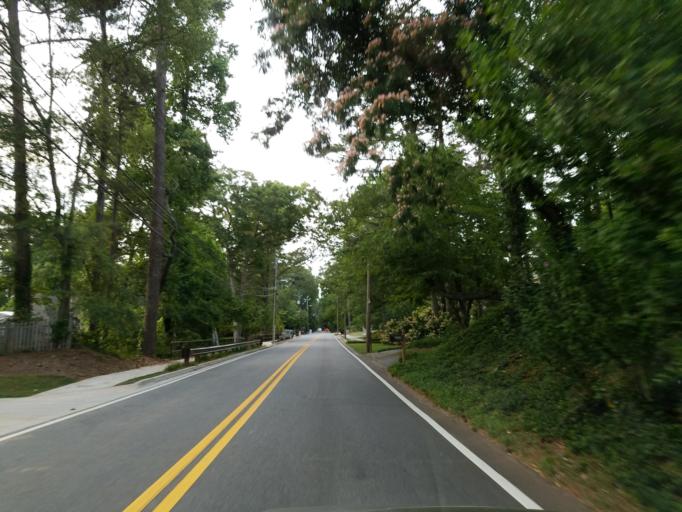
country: US
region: Georgia
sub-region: Fulton County
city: Sandy Springs
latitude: 33.8840
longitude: -84.3971
